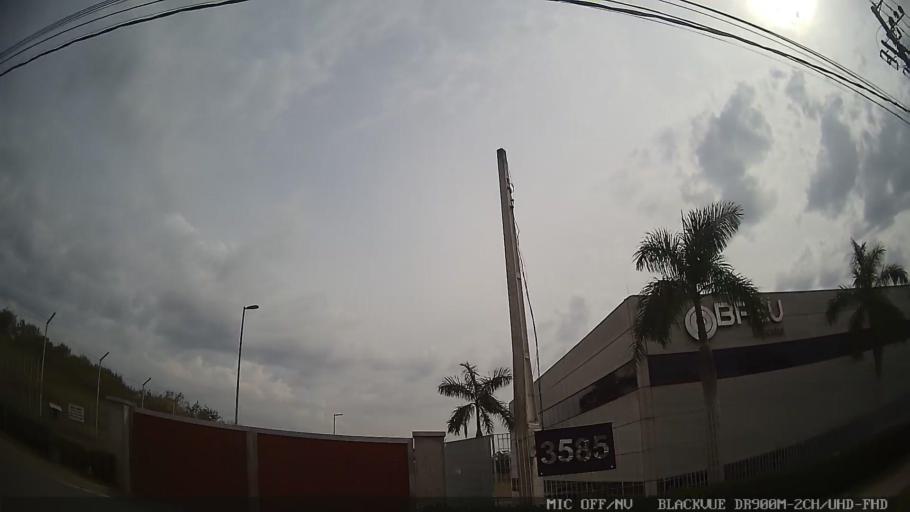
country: BR
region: Sao Paulo
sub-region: Indaiatuba
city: Indaiatuba
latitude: -23.1061
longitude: -47.2769
